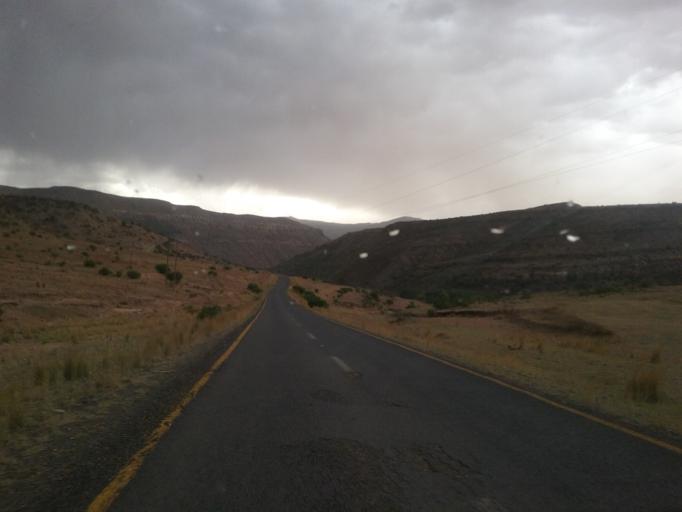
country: LS
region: Quthing
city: Quthing
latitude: -30.2874
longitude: 27.7855
